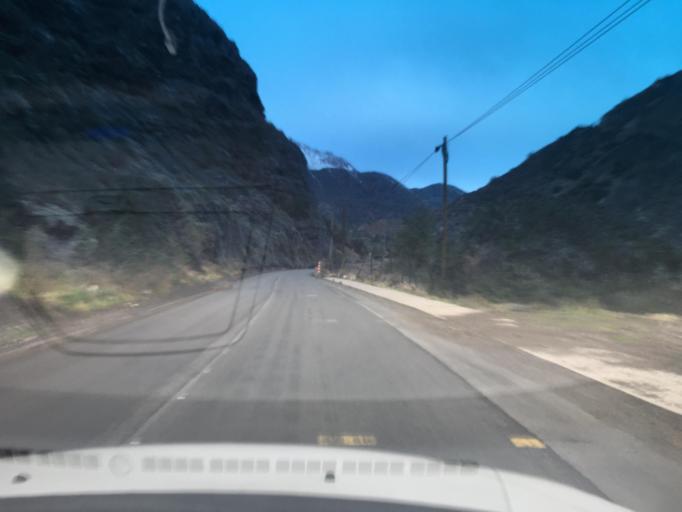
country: CL
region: Santiago Metropolitan
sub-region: Provincia de Cordillera
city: Puente Alto
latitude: -33.7400
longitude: -70.2965
